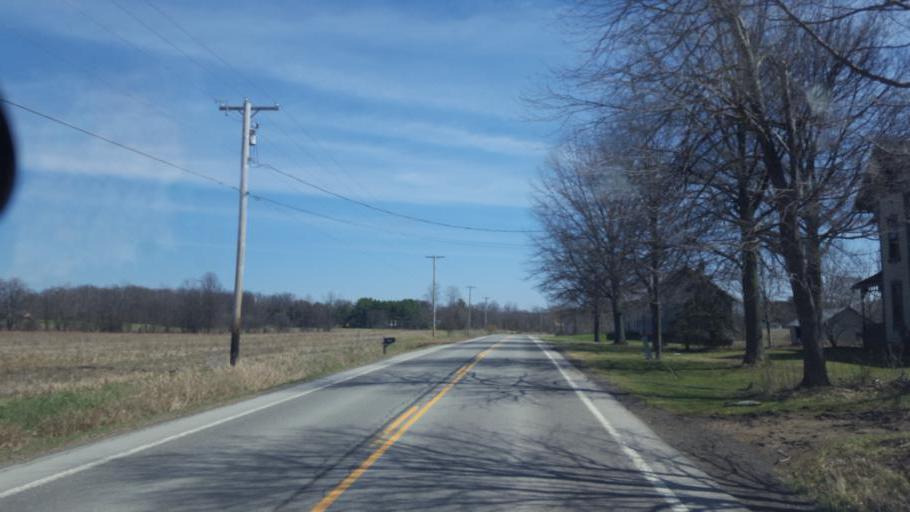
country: US
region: Ohio
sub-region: Ashland County
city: Ashland
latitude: 40.8845
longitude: -82.3758
